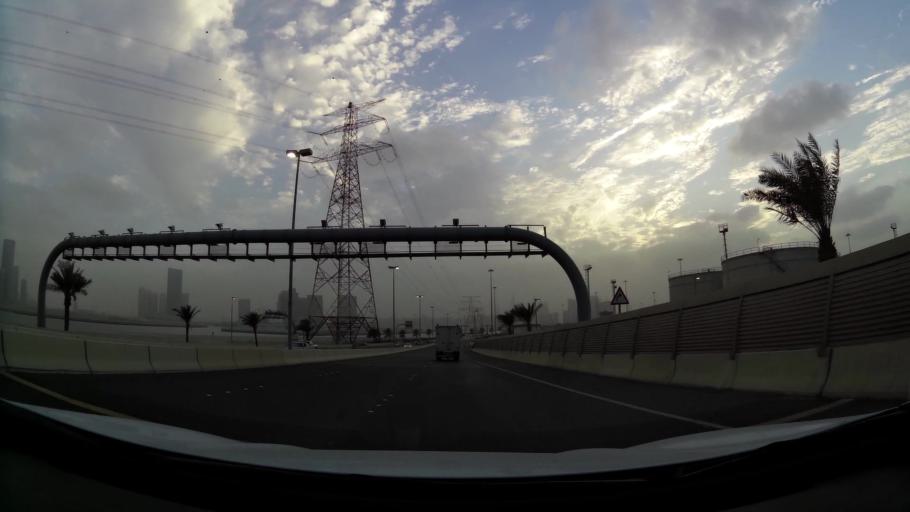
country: AE
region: Abu Dhabi
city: Abu Dhabi
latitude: 24.5176
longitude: 54.3968
